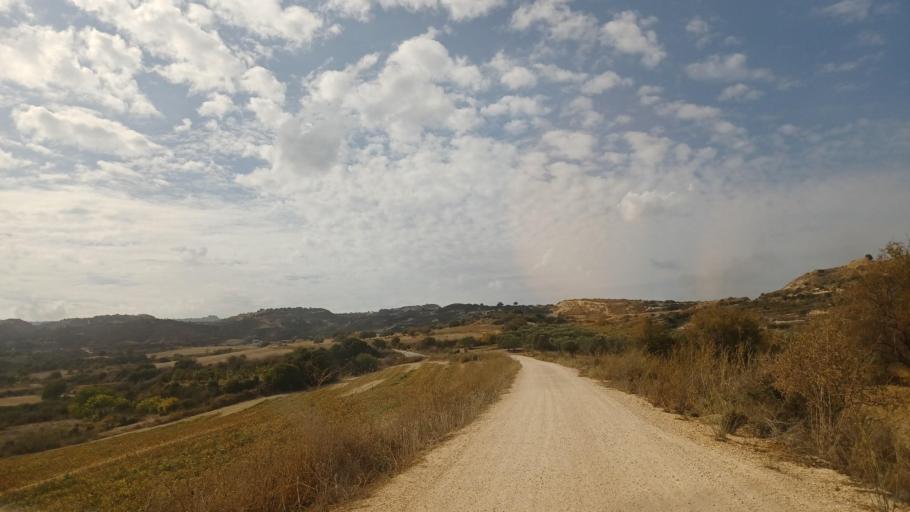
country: CY
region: Pafos
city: Polis
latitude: 35.0172
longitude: 32.4154
